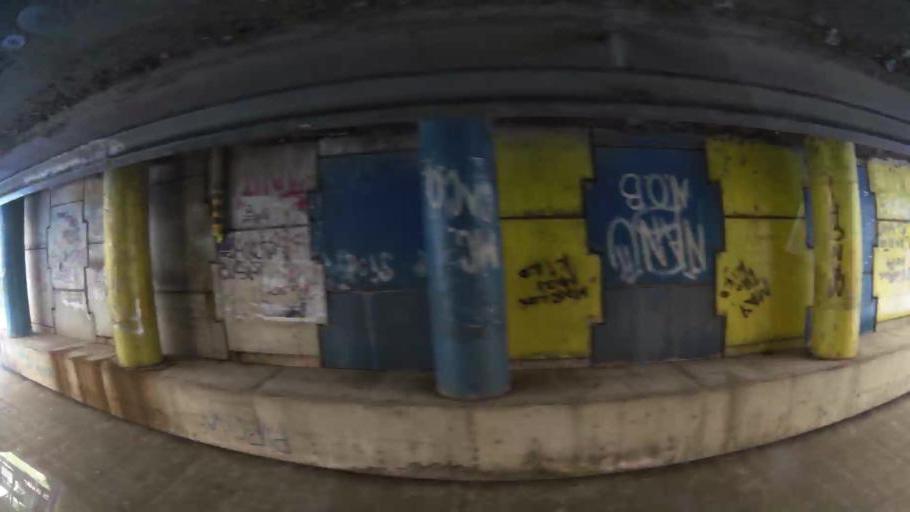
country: AR
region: Santa Fe
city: Perez
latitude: -32.9487
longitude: -60.7191
